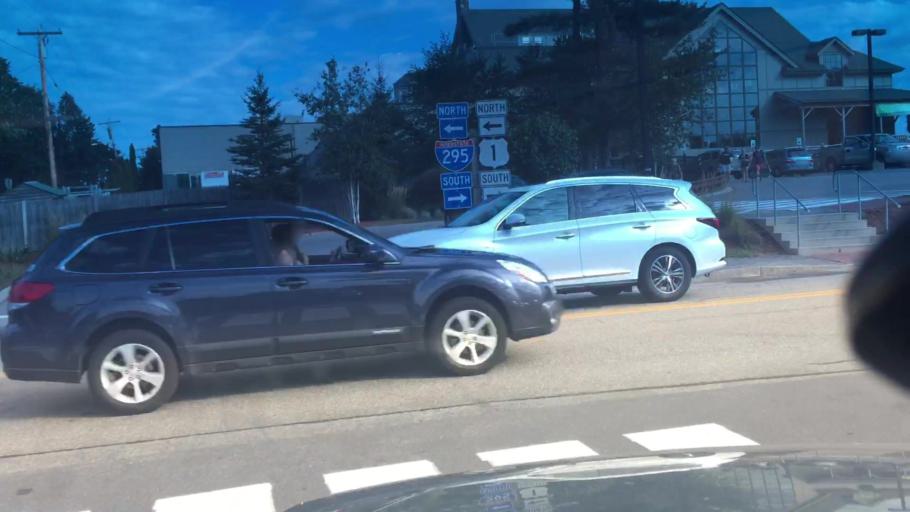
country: US
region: Maine
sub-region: Cumberland County
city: Freeport
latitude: 43.8589
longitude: -70.1050
